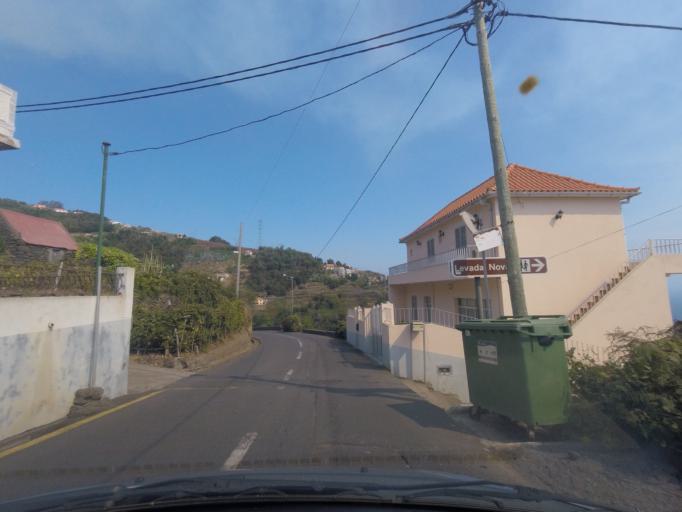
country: PT
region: Madeira
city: Ribeira Brava
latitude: 32.6861
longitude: -17.0662
